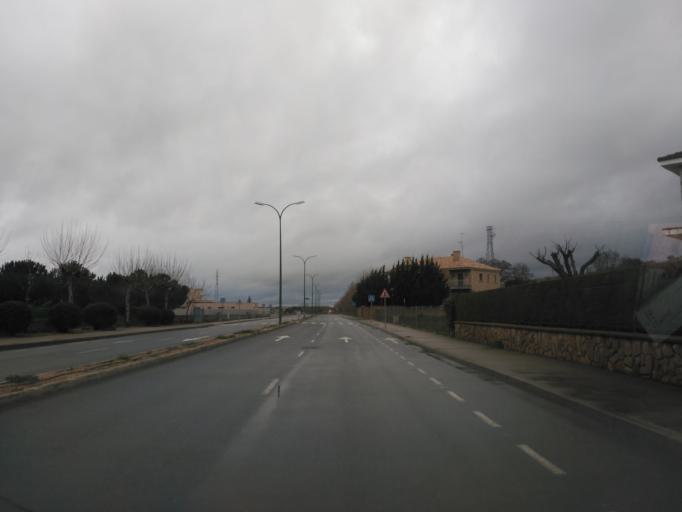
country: ES
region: Castille and Leon
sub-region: Provincia de Salamanca
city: Villamayor
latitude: 40.9848
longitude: -5.7134
